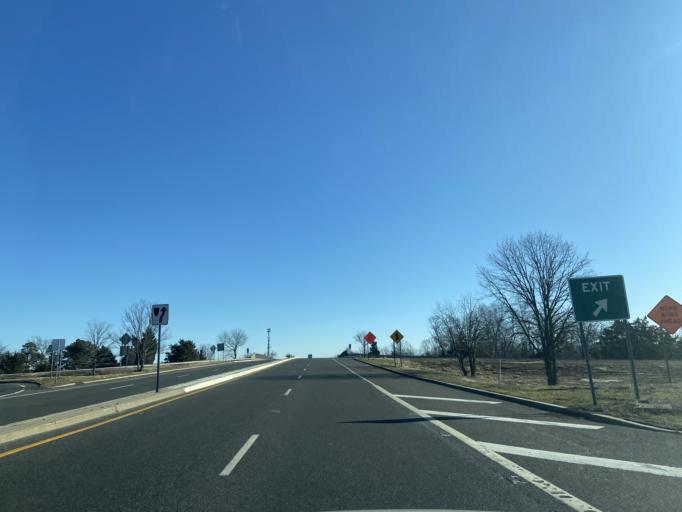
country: US
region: New Jersey
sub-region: Cumberland County
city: Vineland
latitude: 39.4884
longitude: -75.0736
